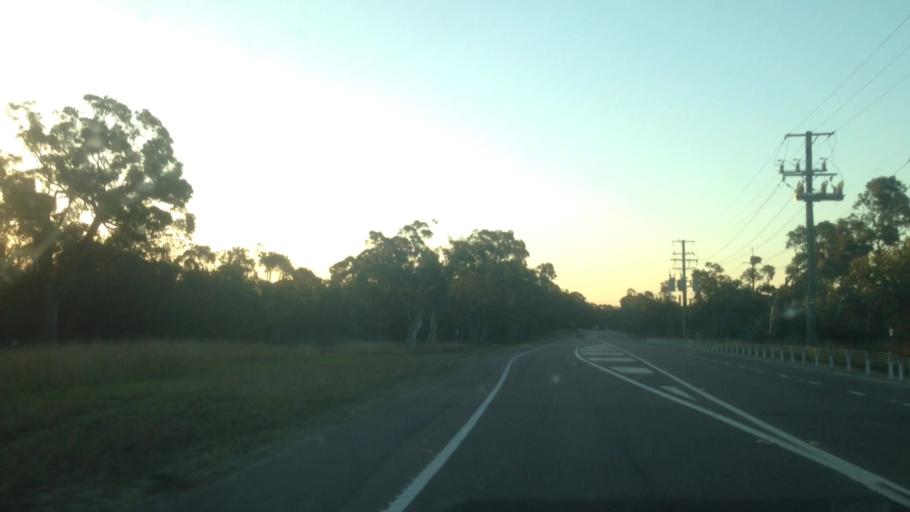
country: AU
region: New South Wales
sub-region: Wyong Shire
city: Kingfisher Shores
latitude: -33.1722
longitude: 151.5380
